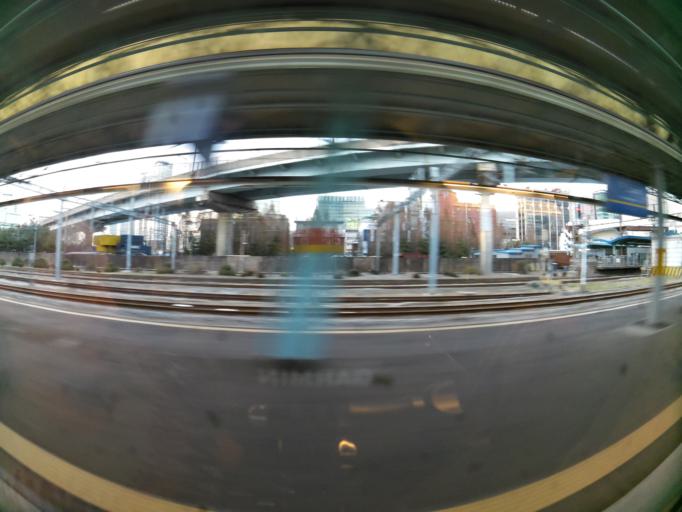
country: KR
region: Gyeonggi-do
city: Kwangmyong
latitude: 37.5146
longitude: 126.9055
